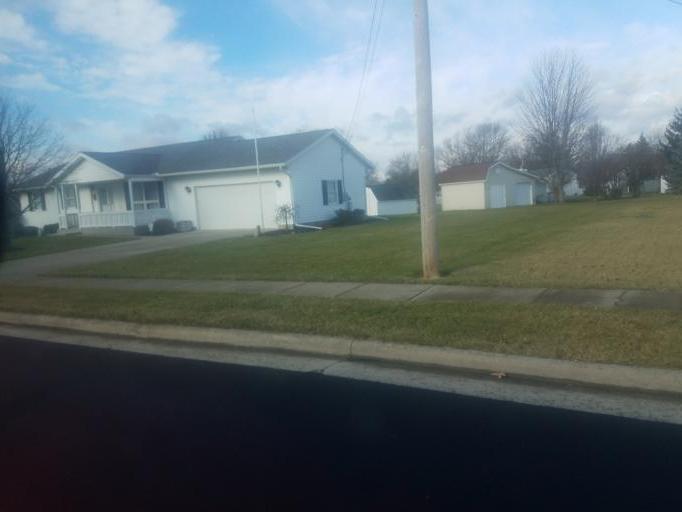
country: US
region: Ohio
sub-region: Marion County
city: Marion
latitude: 40.5697
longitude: -83.1531
